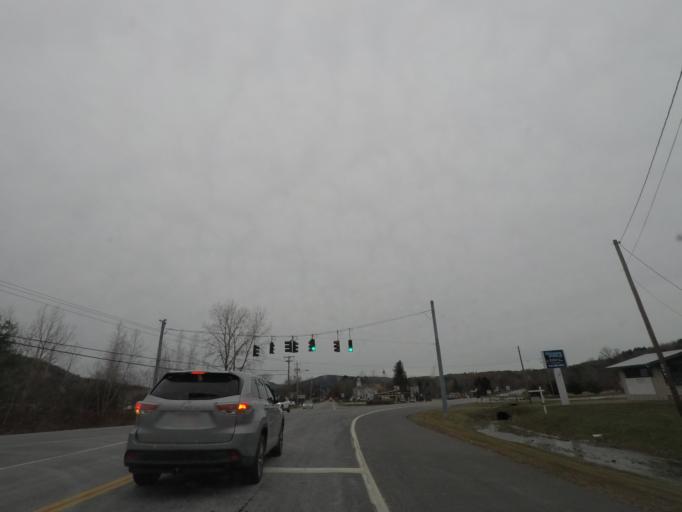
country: US
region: Massachusetts
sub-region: Berkshire County
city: Lanesborough
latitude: 42.5477
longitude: -73.3683
